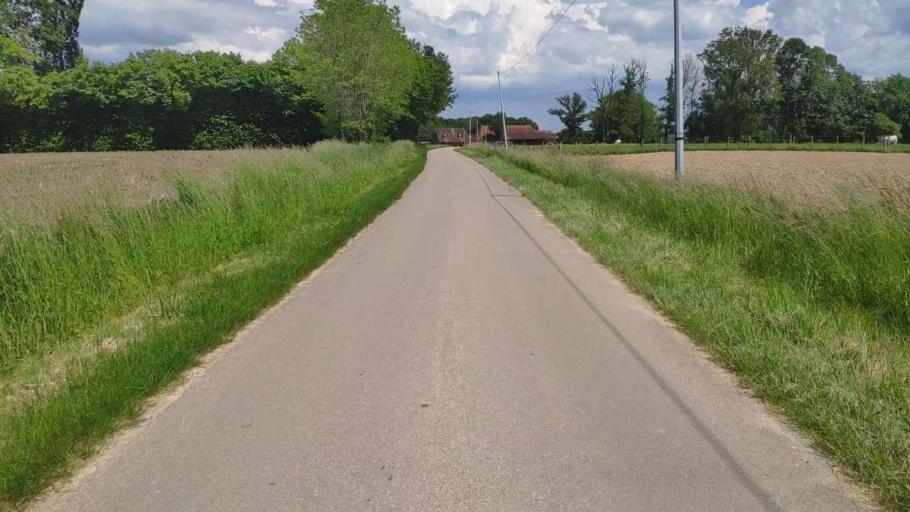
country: FR
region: Franche-Comte
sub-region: Departement du Jura
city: Bletterans
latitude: 46.7885
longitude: 5.4040
